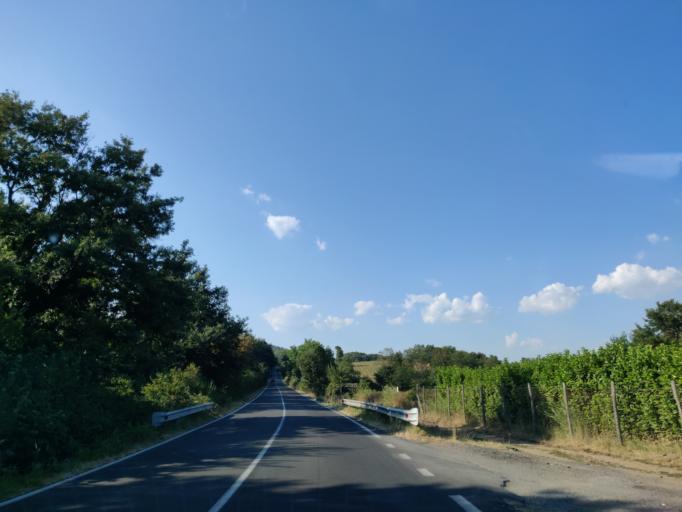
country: IT
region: Latium
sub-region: Provincia di Viterbo
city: Latera
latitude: 42.6057
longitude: 11.8439
